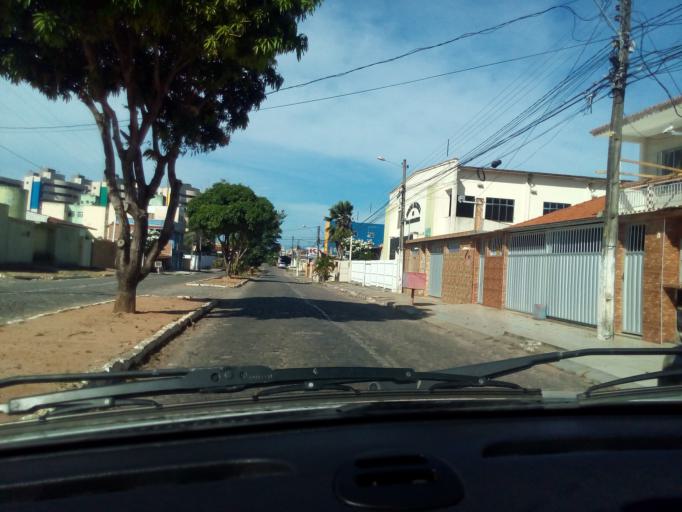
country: BR
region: Rio Grande do Norte
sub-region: Parnamirim
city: Parnamirim
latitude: -5.8815
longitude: -35.2069
